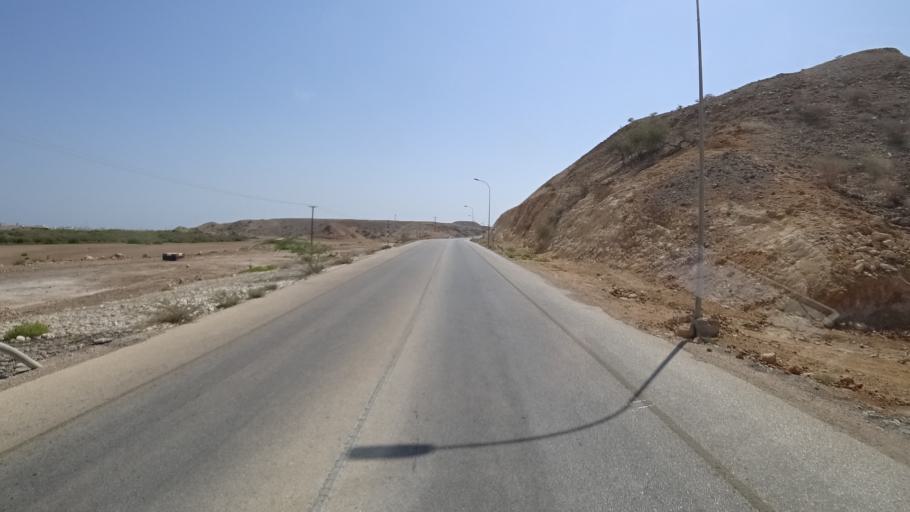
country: OM
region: Ash Sharqiyah
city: Sur
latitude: 22.5427
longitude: 59.5106
